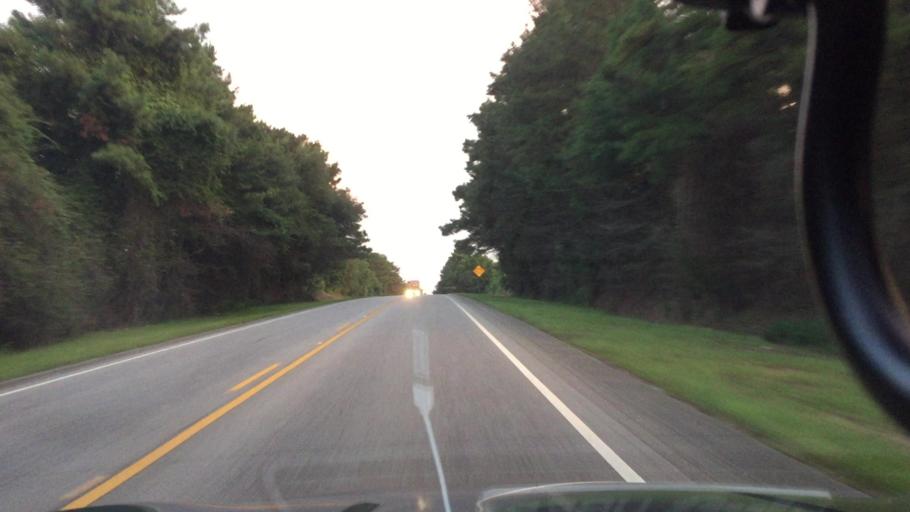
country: US
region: Alabama
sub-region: Coffee County
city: Enterprise
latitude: 31.3692
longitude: -85.8694
